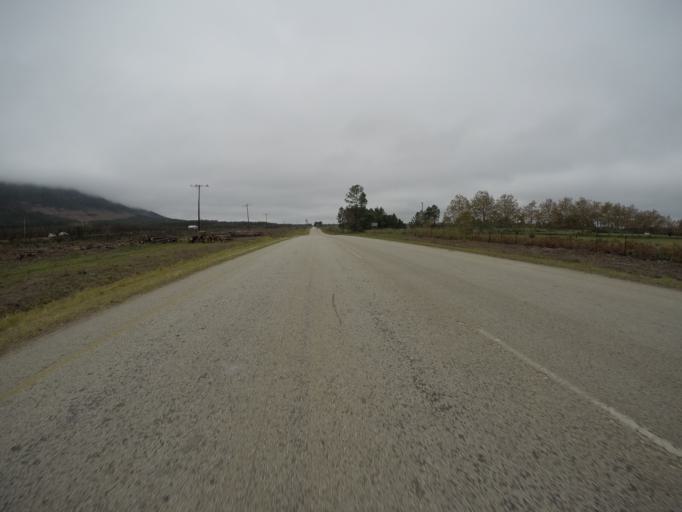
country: ZA
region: Eastern Cape
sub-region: Cacadu District Municipality
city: Kareedouw
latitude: -33.9851
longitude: 24.0637
